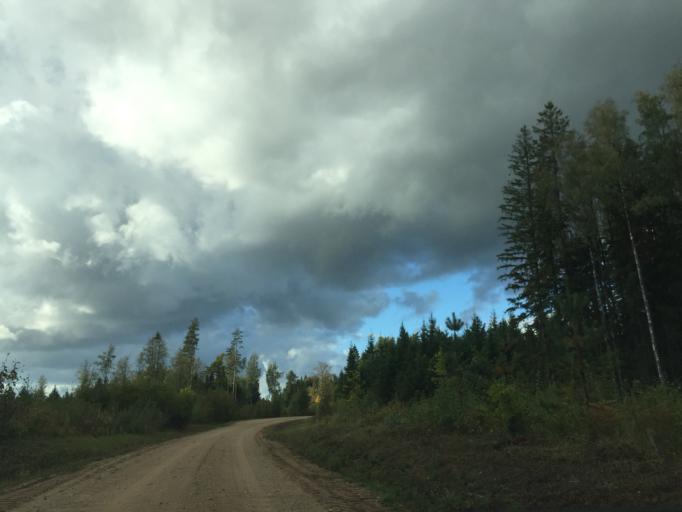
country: LV
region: Ligatne
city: Ligatne
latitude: 57.1034
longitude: 25.1350
